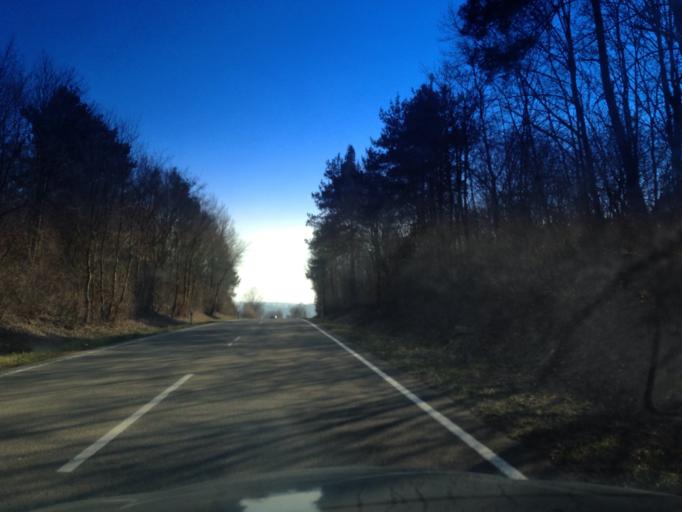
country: DE
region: Baden-Wuerttemberg
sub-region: Karlsruhe Region
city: Illingen
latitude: 48.9432
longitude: 8.9087
